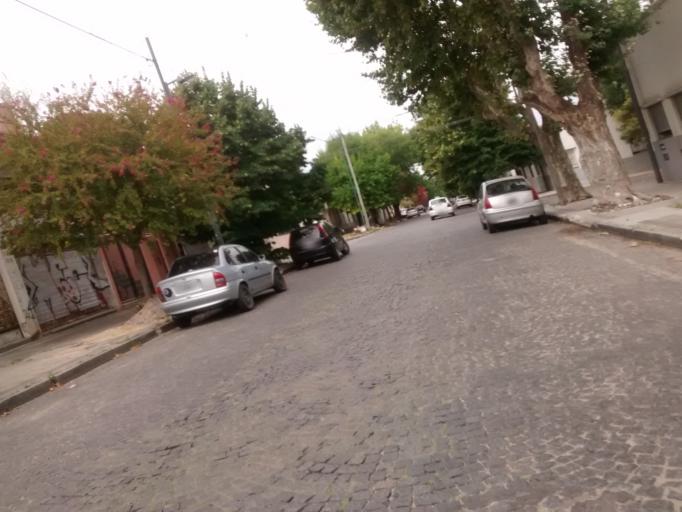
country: AR
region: Buenos Aires
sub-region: Partido de La Plata
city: La Plata
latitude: -34.9272
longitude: -57.9286
